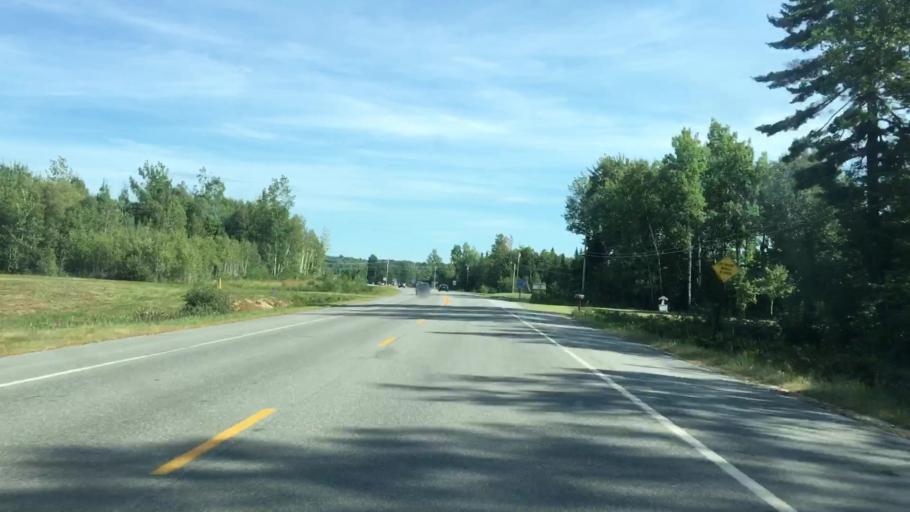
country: US
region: Maine
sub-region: Penobscot County
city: Lincoln
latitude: 45.3591
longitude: -68.5438
